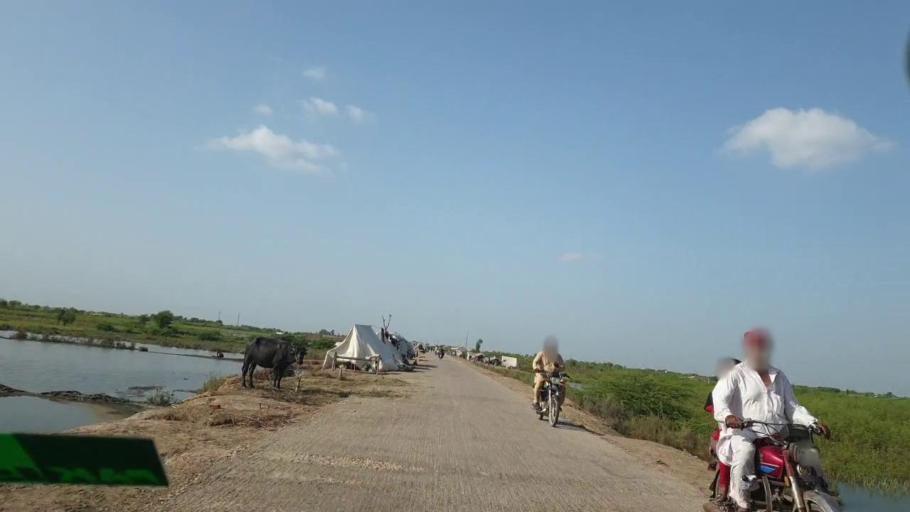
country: PK
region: Sindh
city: Naukot
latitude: 24.7434
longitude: 69.1980
